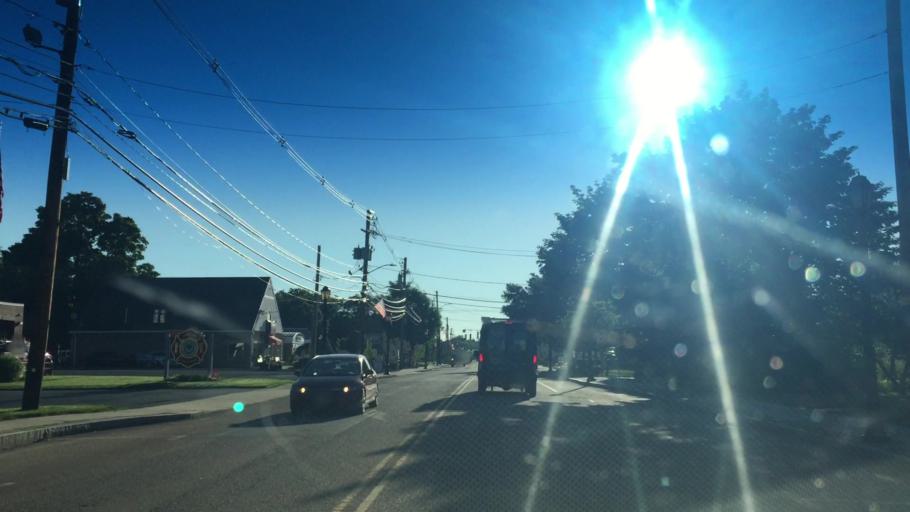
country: US
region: Massachusetts
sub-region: Norfolk County
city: Millis
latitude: 42.1667
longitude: -71.3591
